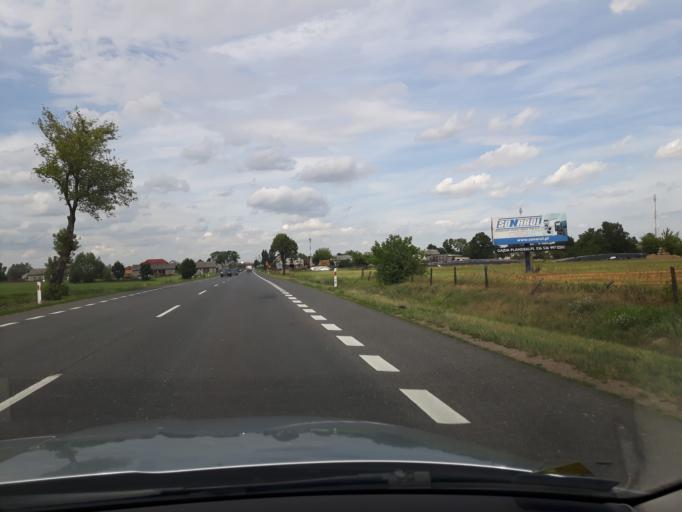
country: PL
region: Masovian Voivodeship
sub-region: Powiat mlawski
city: Strzegowo
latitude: 52.9377
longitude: 20.2834
